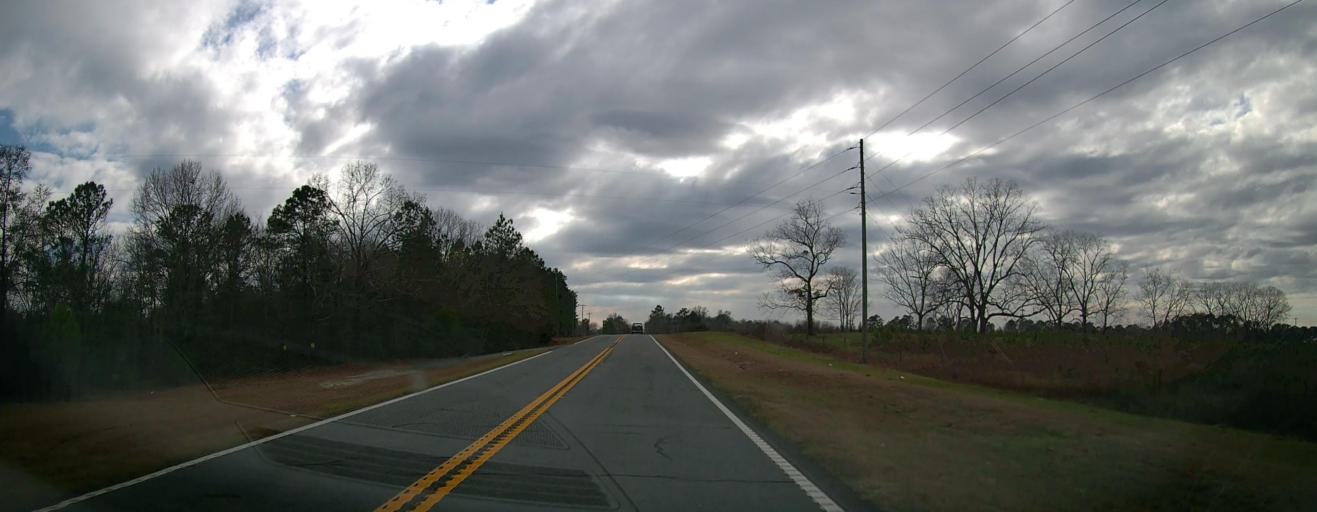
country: US
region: Georgia
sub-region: Marion County
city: Buena Vista
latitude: 32.4105
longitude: -84.4036
